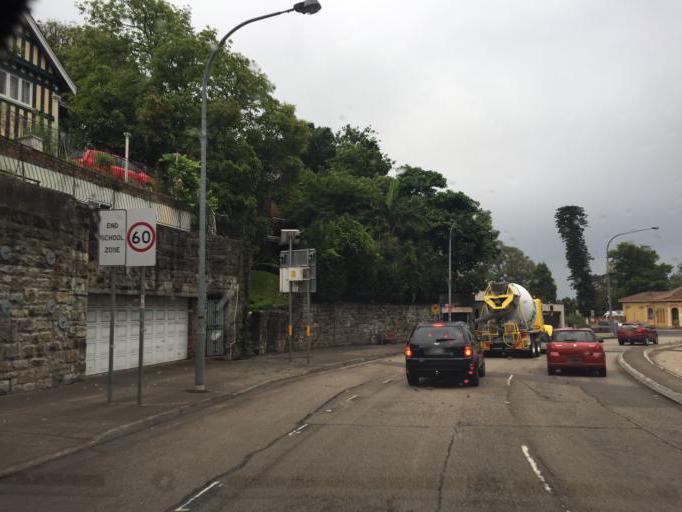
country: AU
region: New South Wales
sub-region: Woollahra
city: Point Piper
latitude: -33.8704
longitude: 151.2517
